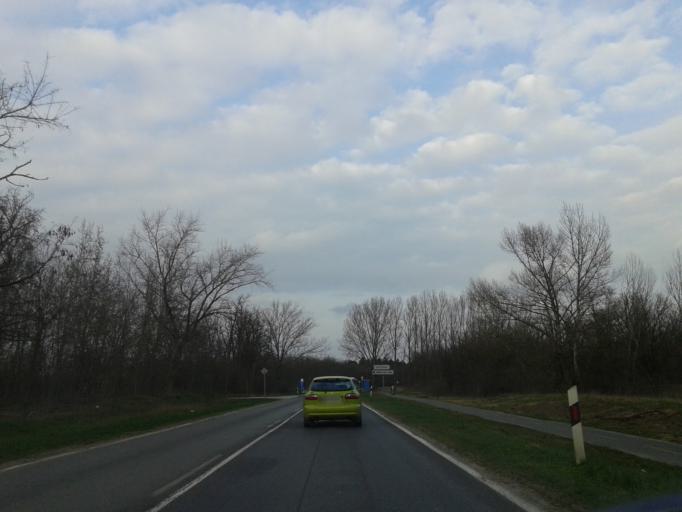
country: HU
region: Gyor-Moson-Sopron
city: Gyor
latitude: 47.7200
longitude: 17.6902
